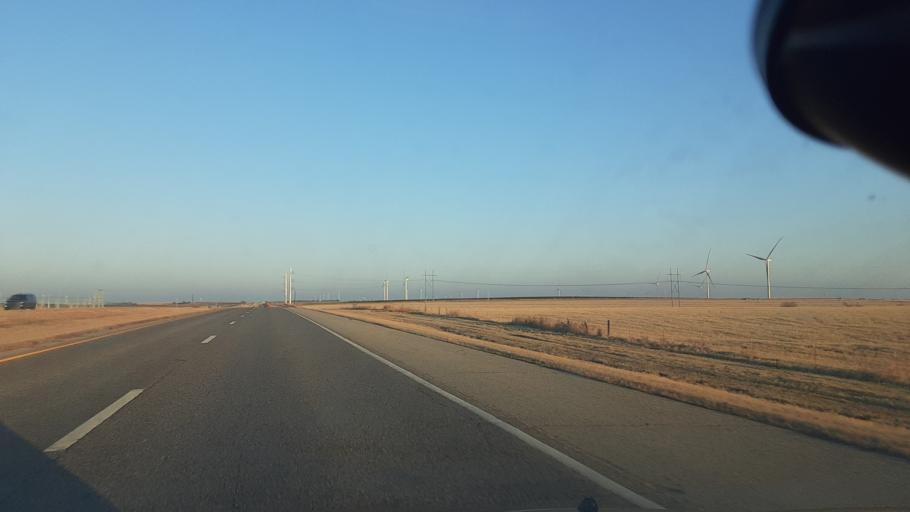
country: US
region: Oklahoma
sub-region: Noble County
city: Perry
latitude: 36.3976
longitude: -97.4855
